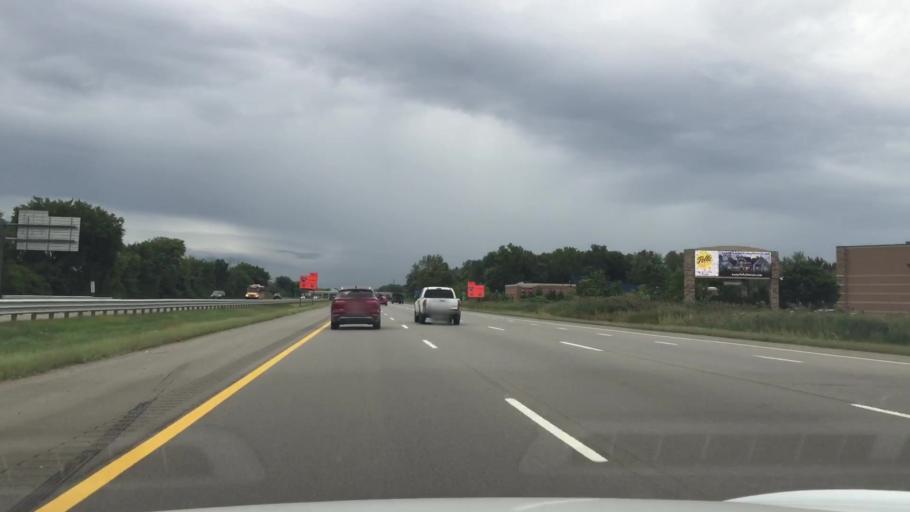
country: US
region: Michigan
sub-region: Macomb County
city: New Haven
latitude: 42.6693
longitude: -82.8260
